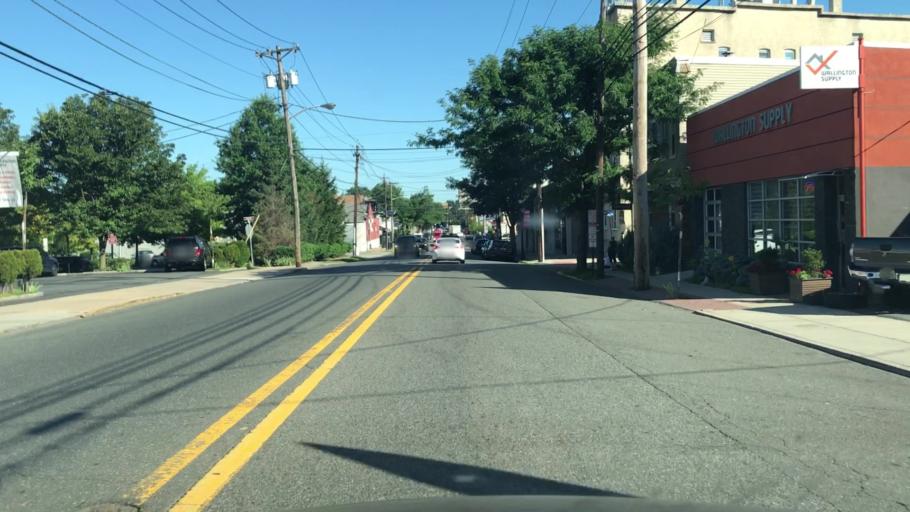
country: US
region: New Jersey
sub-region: Bergen County
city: Wallington
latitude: 40.8479
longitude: -74.1124
